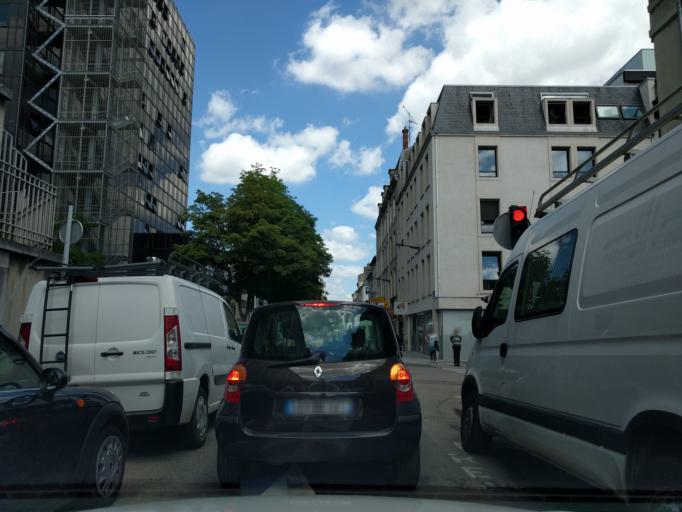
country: FR
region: Lorraine
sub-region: Departement de Meurthe-et-Moselle
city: Nancy
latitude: 48.6871
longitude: 6.1828
